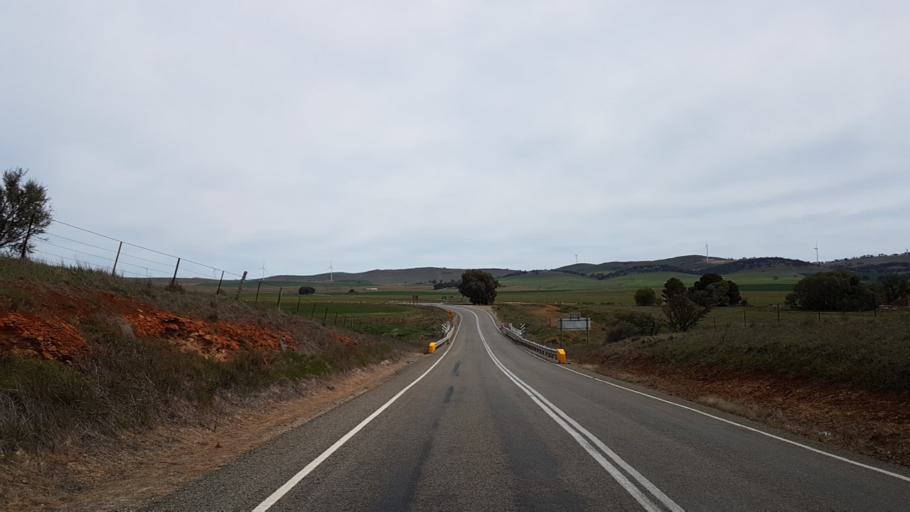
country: AU
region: South Australia
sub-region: Northern Areas
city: Jamestown
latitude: -33.0435
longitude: 138.6220
